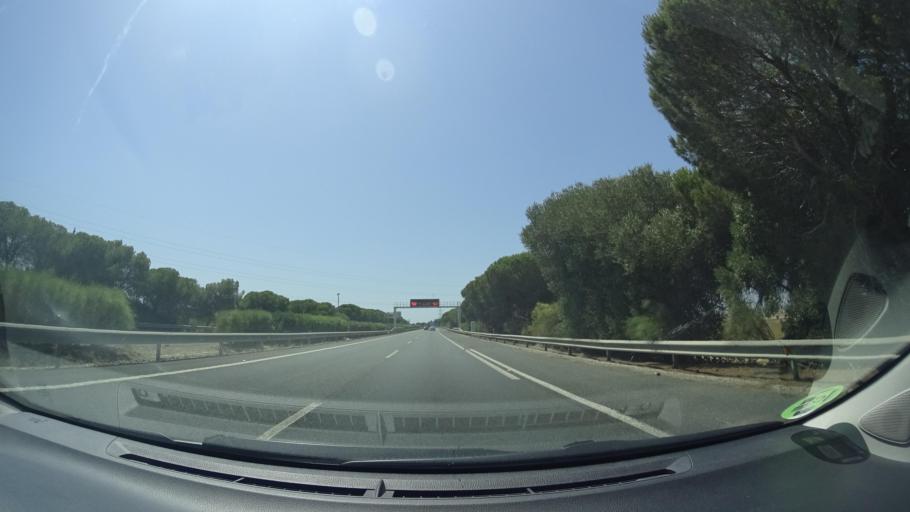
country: ES
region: Andalusia
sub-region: Provincia de Cadiz
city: Puerto Real
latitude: 36.5412
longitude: -6.1761
